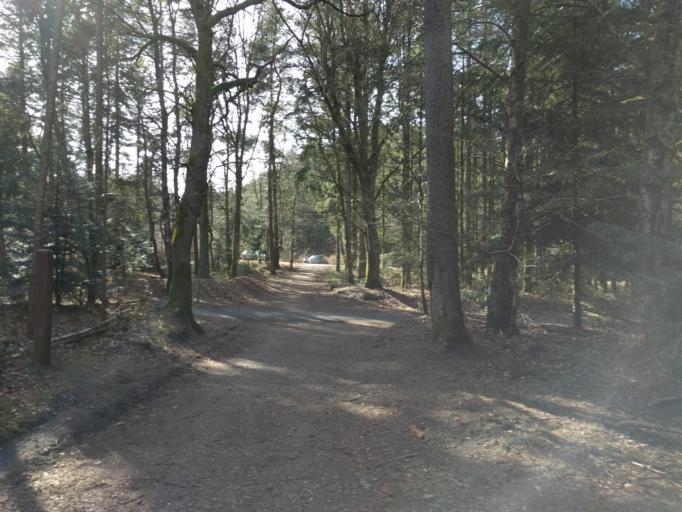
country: DK
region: Central Jutland
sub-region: Silkeborg Kommune
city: Silkeborg
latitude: 56.1702
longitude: 9.5292
